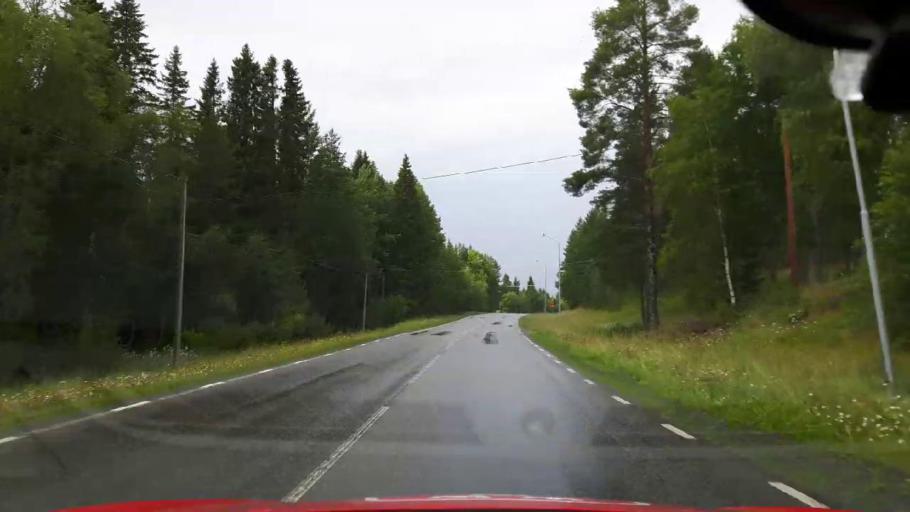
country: SE
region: Jaemtland
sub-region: Krokoms Kommun
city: Krokom
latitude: 63.3286
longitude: 14.2903
